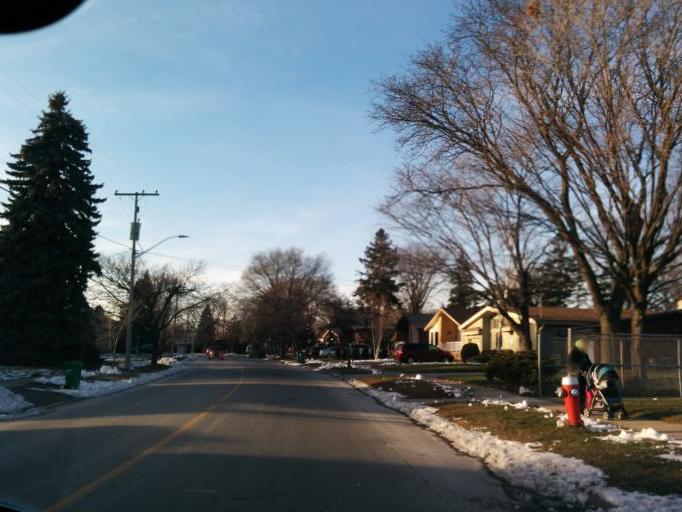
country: CA
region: Ontario
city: Etobicoke
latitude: 43.6067
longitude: -79.5959
